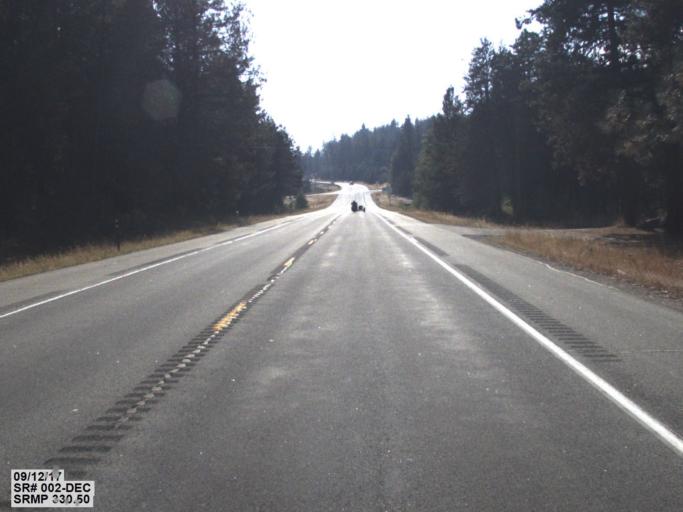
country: US
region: Washington
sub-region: Pend Oreille County
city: Newport
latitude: 48.1538
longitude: -117.1048
